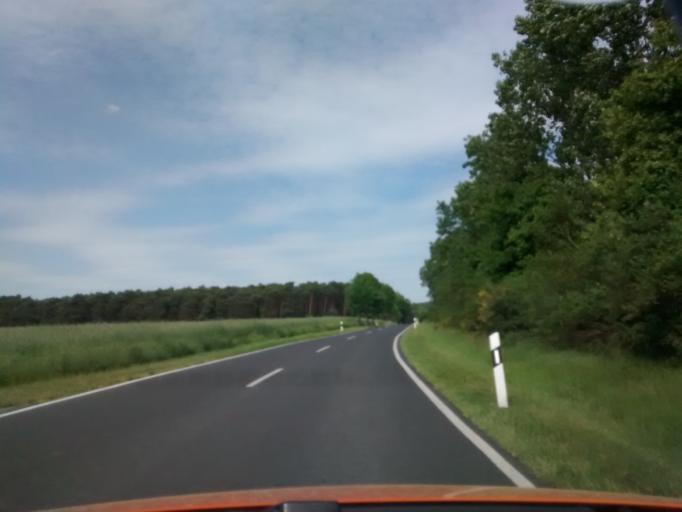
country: DE
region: Brandenburg
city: Ihlow
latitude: 51.9038
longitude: 13.3159
